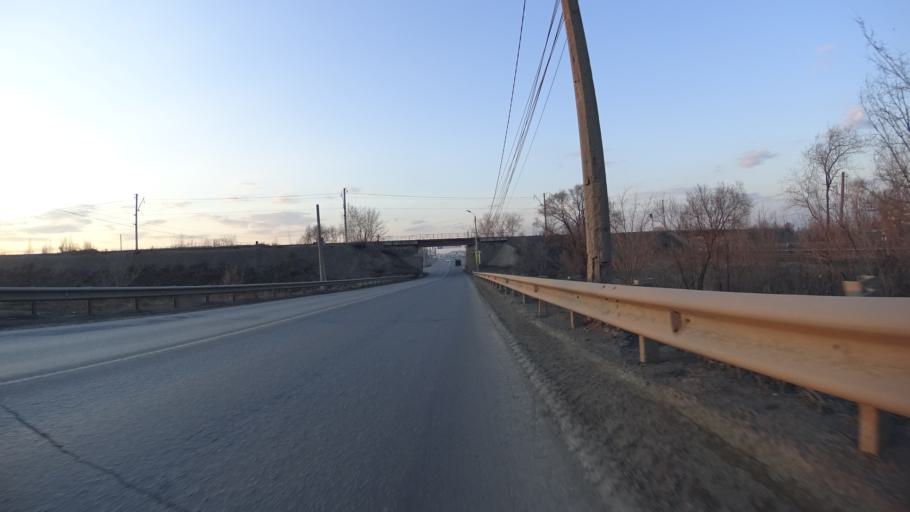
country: RU
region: Chelyabinsk
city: Novosineglazovskiy
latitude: 55.0830
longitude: 61.3882
